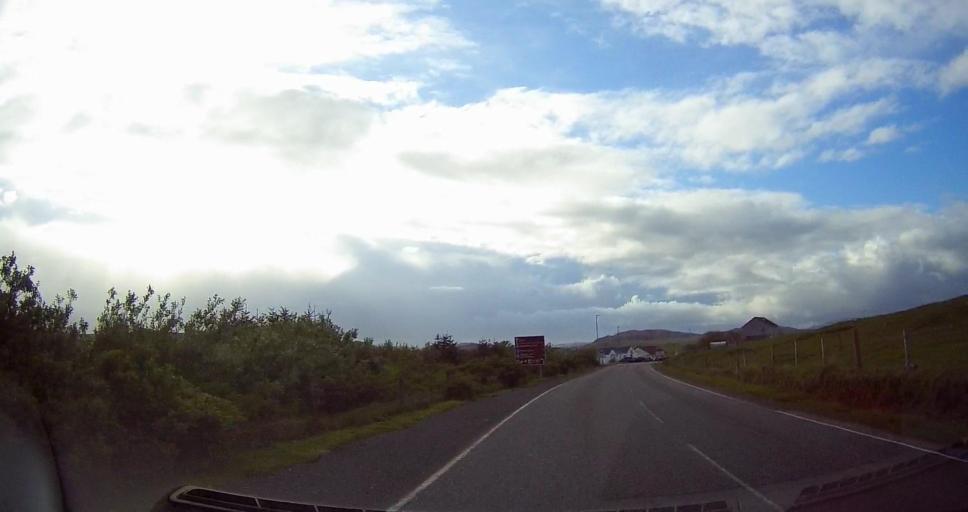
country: GB
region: Scotland
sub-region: Shetland Islands
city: Lerwick
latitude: 60.3868
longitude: -1.3465
